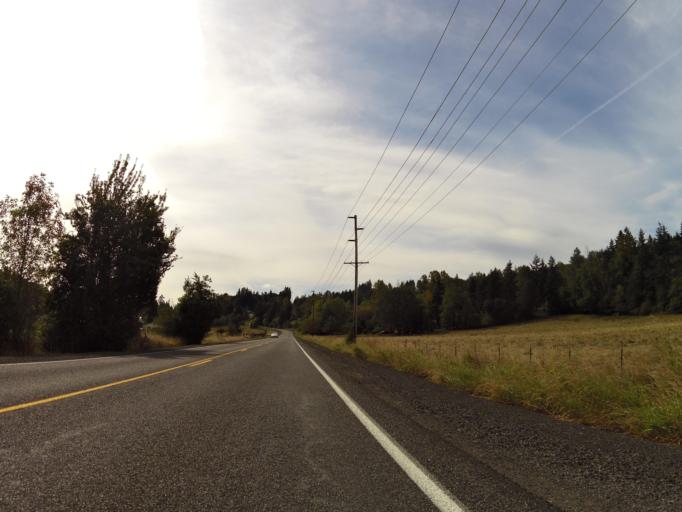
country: US
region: Washington
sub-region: Lewis County
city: Chehalis
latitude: 46.6396
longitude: -122.9713
